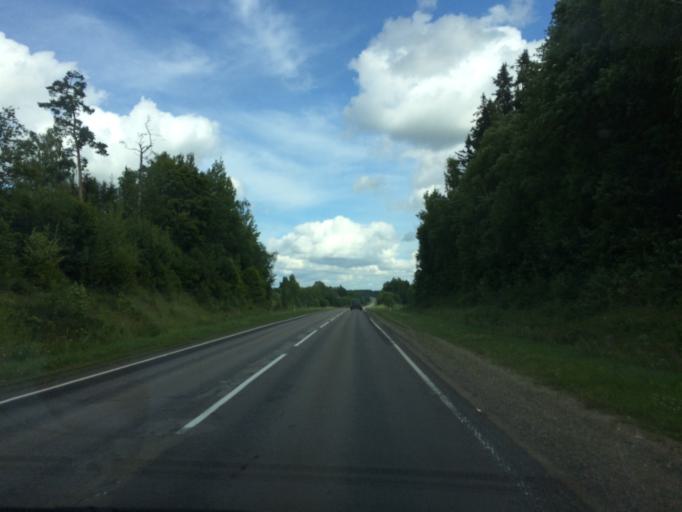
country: LV
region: Rezekne
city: Rezekne
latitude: 56.5990
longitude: 27.4226
